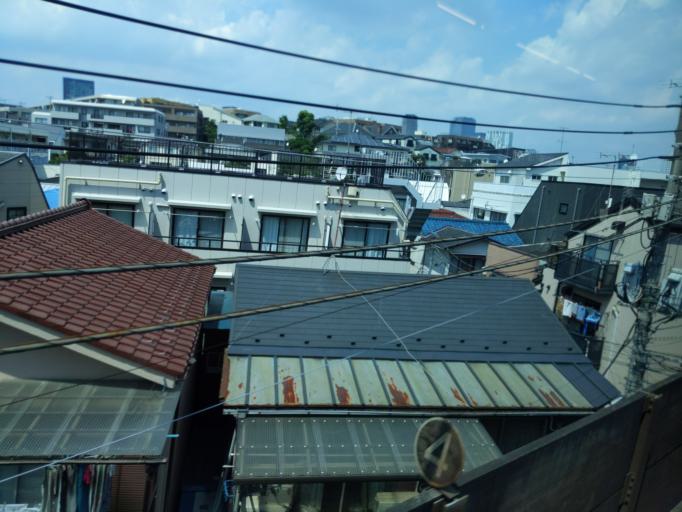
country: JP
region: Tokyo
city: Tokyo
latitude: 35.6414
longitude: 139.6951
